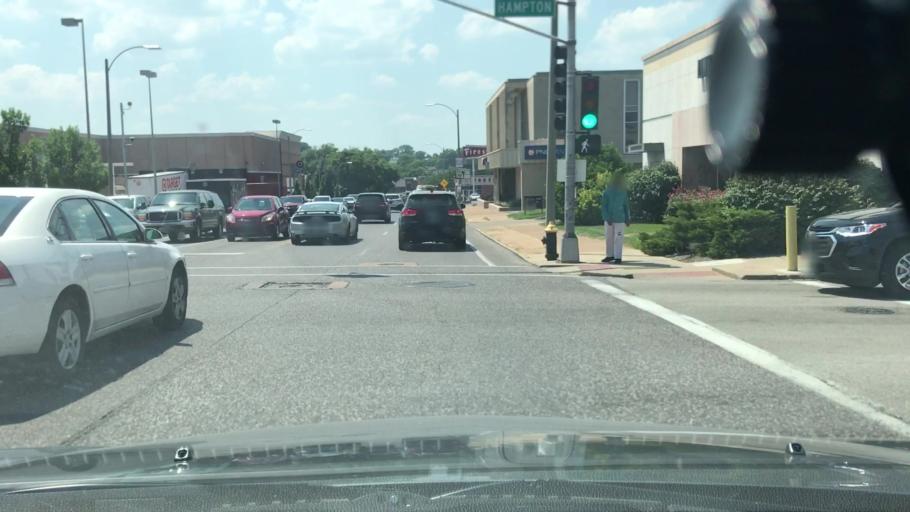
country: US
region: Missouri
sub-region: Saint Louis County
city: Maplewood
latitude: 38.5935
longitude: -90.2942
